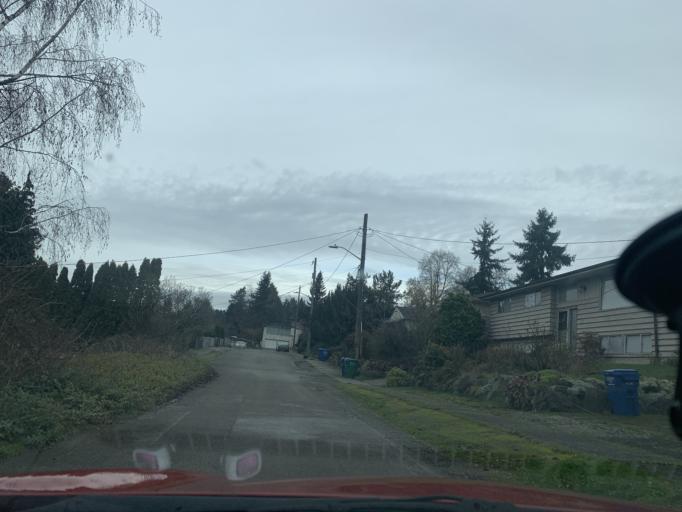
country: US
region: Washington
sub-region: King County
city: Bryn Mawr-Skyway
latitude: 47.5307
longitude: -122.2676
